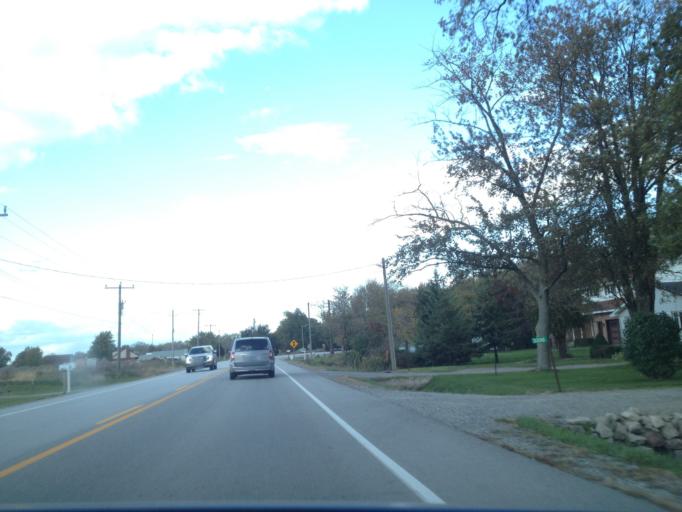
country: CA
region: Ontario
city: Amherstburg
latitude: 42.0955
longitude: -82.7354
